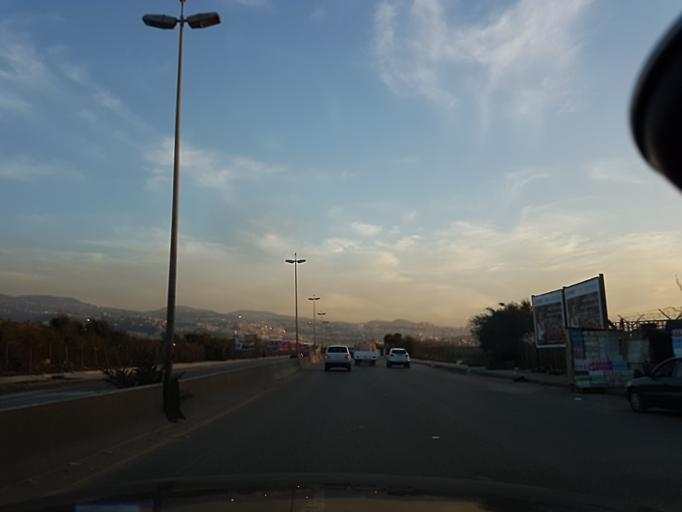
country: LB
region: Mont-Liban
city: Baabda
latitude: 33.8284
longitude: 35.4844
